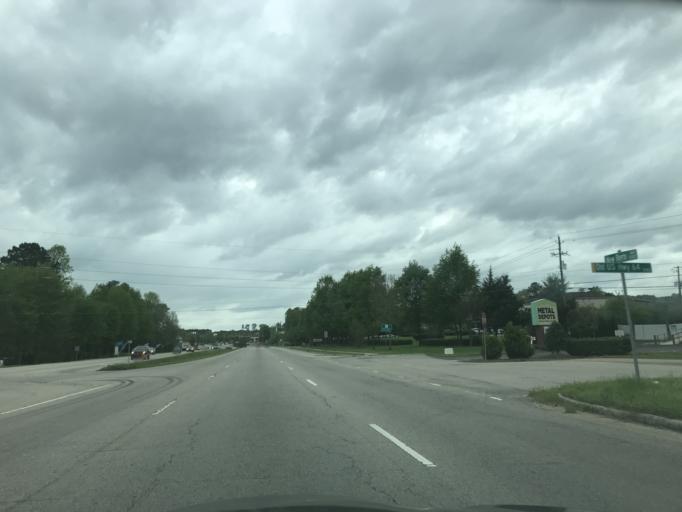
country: US
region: North Carolina
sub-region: Wake County
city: Knightdale
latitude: 35.7948
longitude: -78.5502
